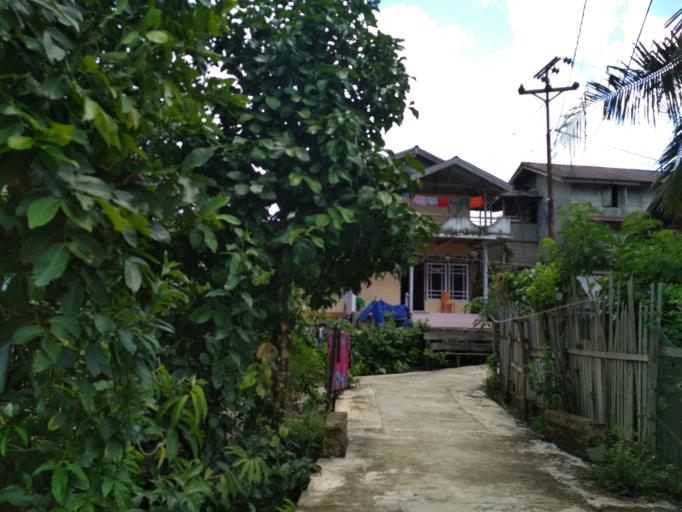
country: ID
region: West Kalimantan
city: Bengkayang
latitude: 0.7523
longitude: 110.1011
